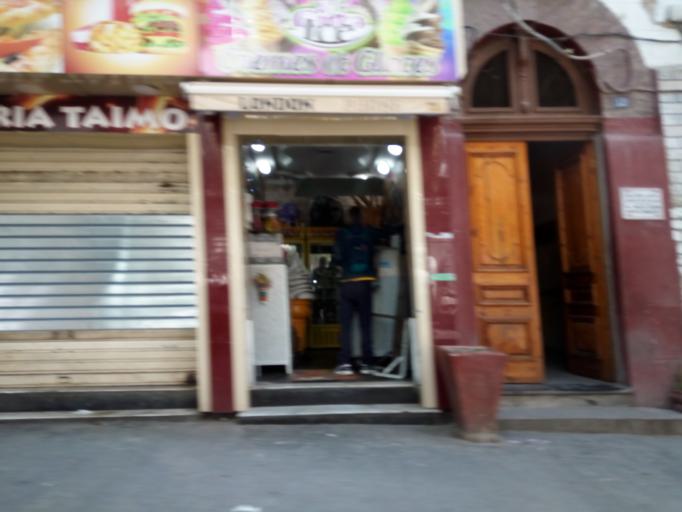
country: DZ
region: Constantine
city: Constantine
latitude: 36.3624
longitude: 6.6043
